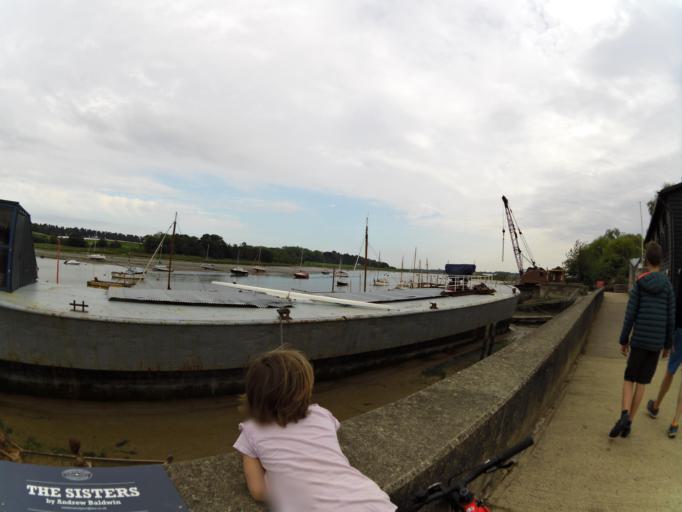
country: GB
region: England
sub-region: Suffolk
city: Woodbridge
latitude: 52.0885
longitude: 1.3168
